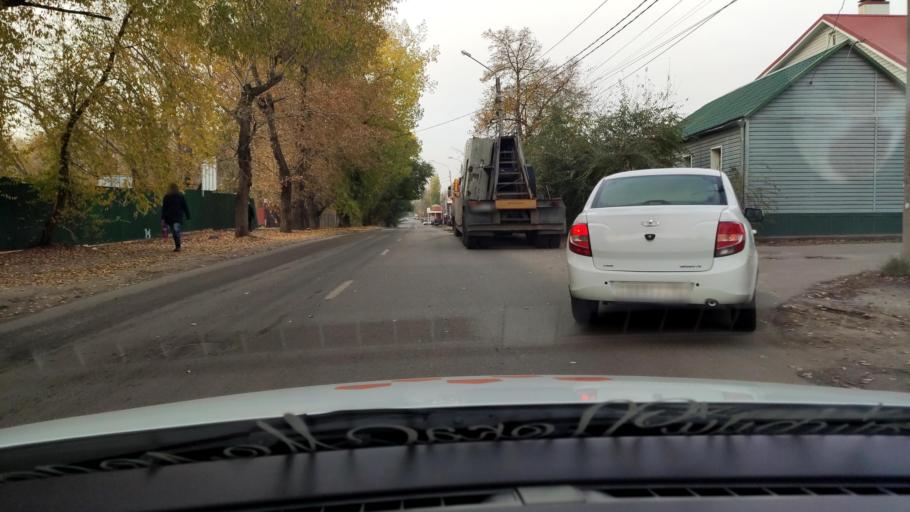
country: RU
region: Voronezj
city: Voronezh
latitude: 51.6646
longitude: 39.1665
